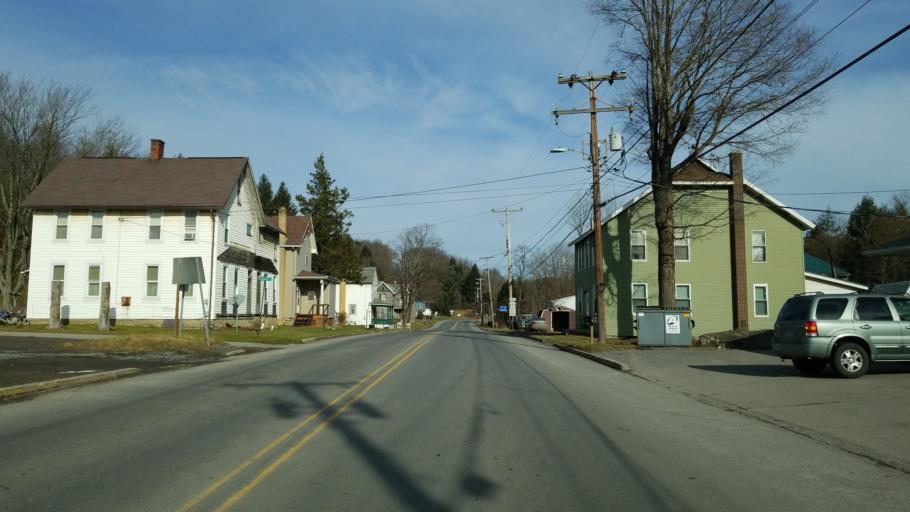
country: US
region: Pennsylvania
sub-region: Clearfield County
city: Curwensville
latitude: 40.9644
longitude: -78.6095
